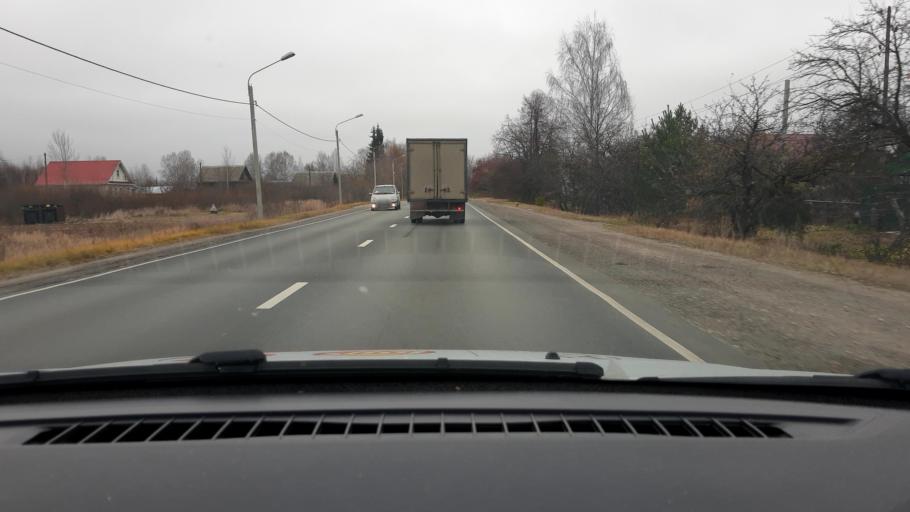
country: RU
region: Nizjnij Novgorod
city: Gorodets
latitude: 56.6049
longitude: 43.4481
